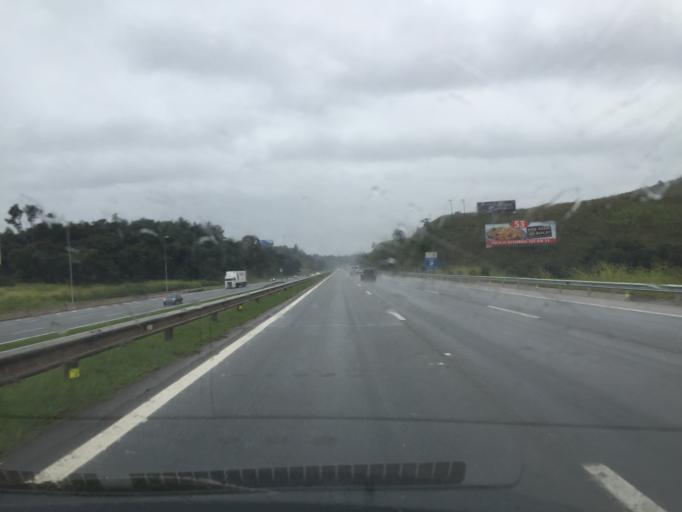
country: BR
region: Sao Paulo
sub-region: Sao Roque
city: Sao Roque
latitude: -23.4226
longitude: -47.1607
